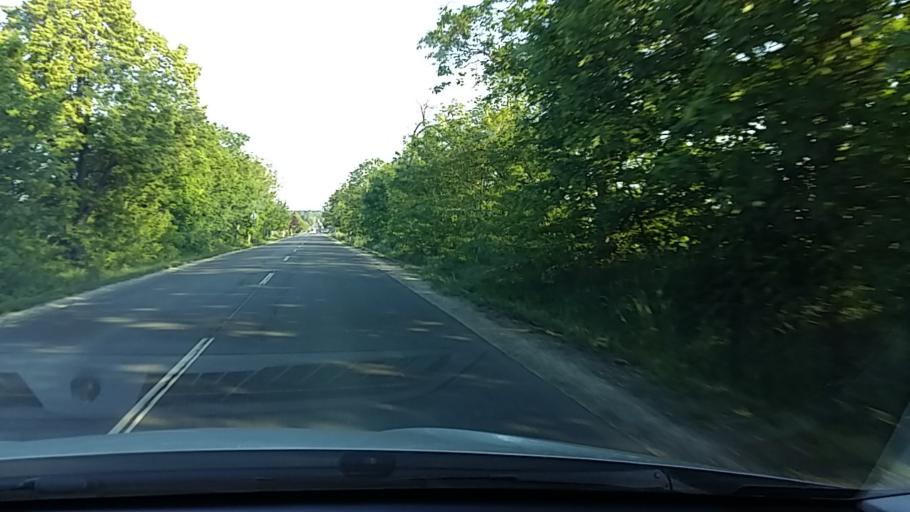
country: HU
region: Pest
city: Szod
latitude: 47.7246
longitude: 19.2277
